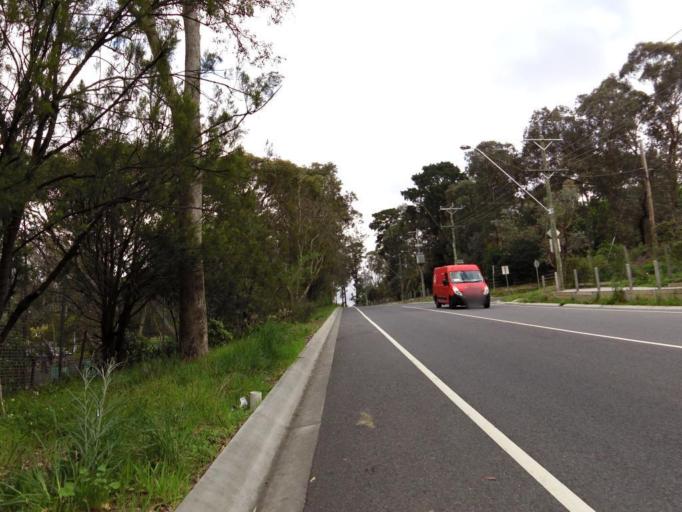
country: AU
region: Victoria
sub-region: Manningham
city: Park Orchards
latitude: -37.7897
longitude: 145.1985
